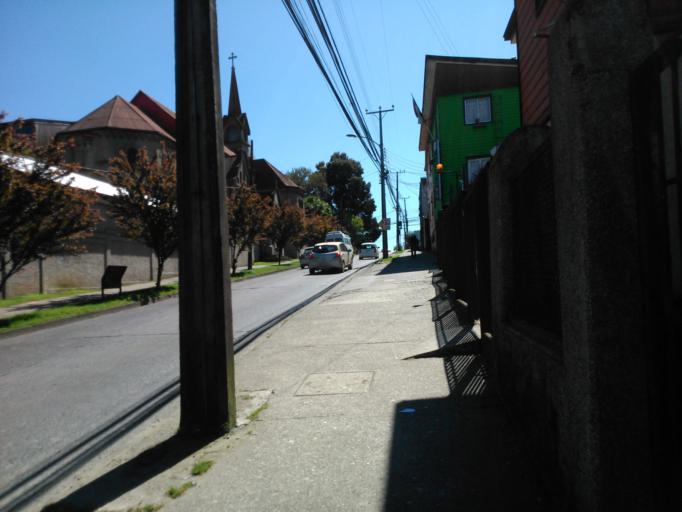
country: CL
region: Los Rios
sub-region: Provincia de Valdivia
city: Valdivia
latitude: -39.8187
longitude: -73.2475
